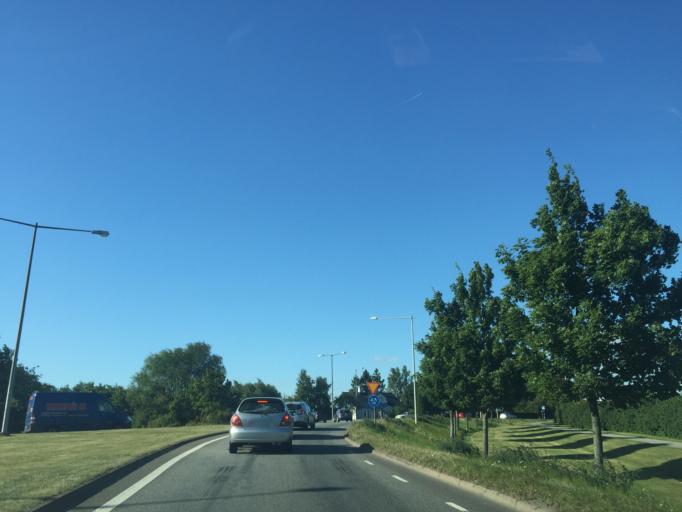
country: SE
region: Skane
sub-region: Ystads Kommun
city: Ystad
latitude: 55.4425
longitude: 13.8354
